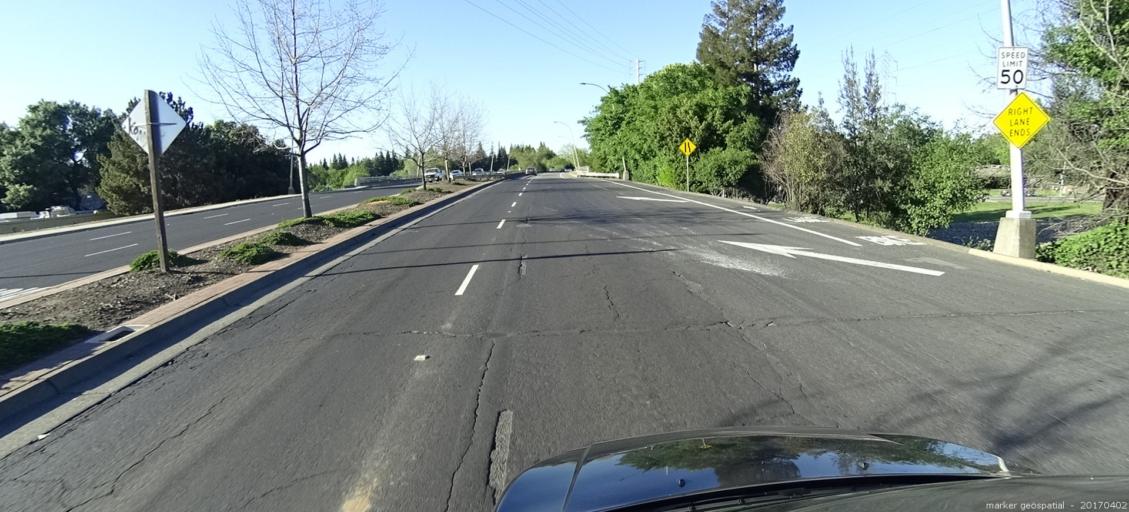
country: US
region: California
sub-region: Sacramento County
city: Rosemont
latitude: 38.5568
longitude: -121.4093
